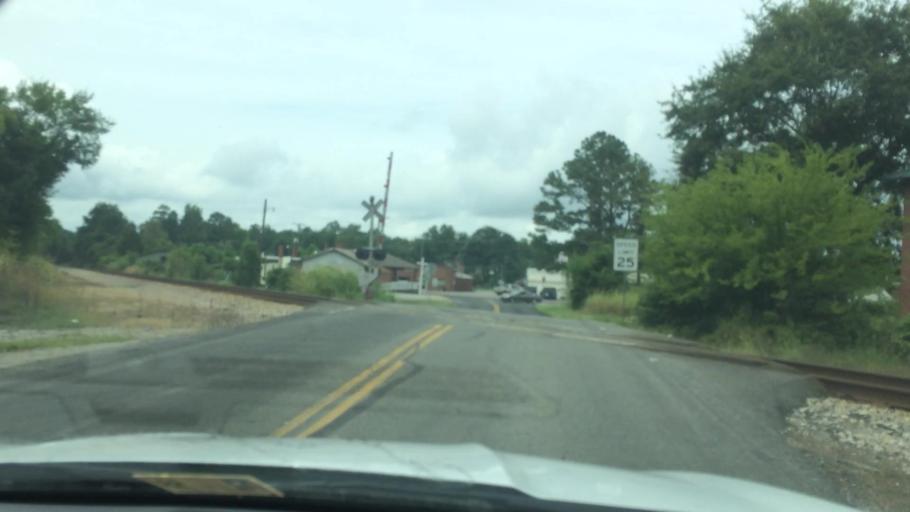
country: US
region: Virginia
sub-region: New Kent County
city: New Kent
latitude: 37.4410
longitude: -77.0414
